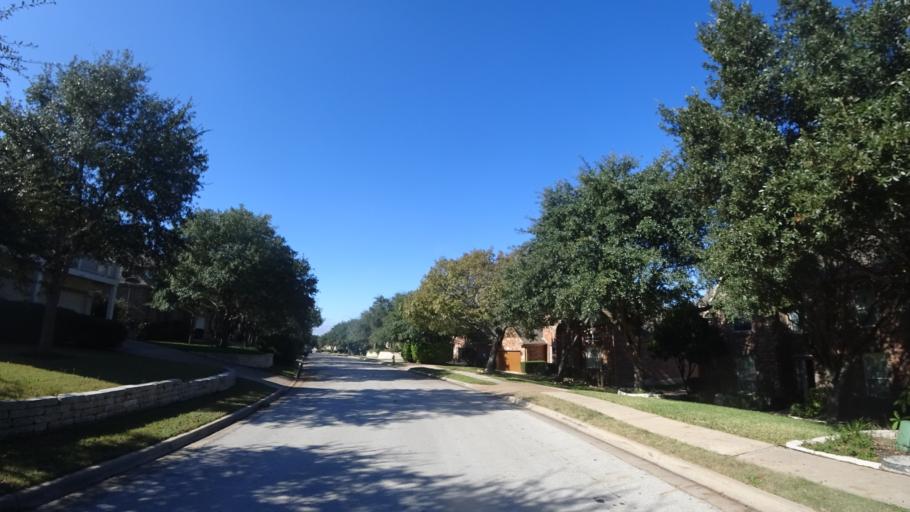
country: US
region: Texas
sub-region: Travis County
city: Hudson Bend
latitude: 30.3776
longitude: -97.8964
